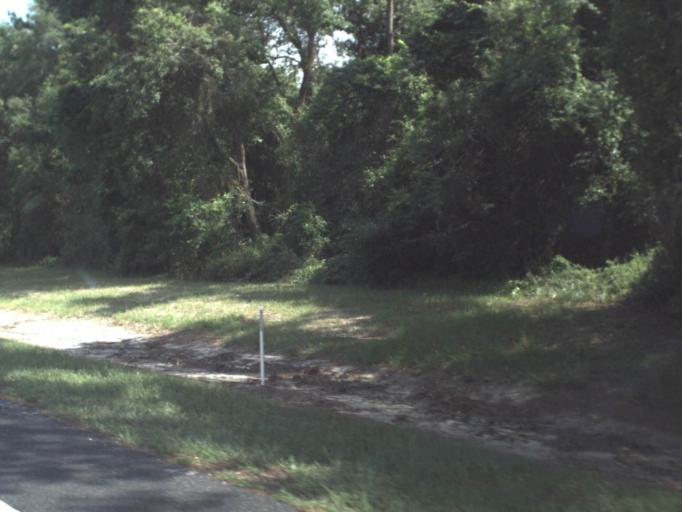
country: US
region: Florida
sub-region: Saint Johns County
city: Fruit Cove
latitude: 30.1473
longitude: -81.5219
